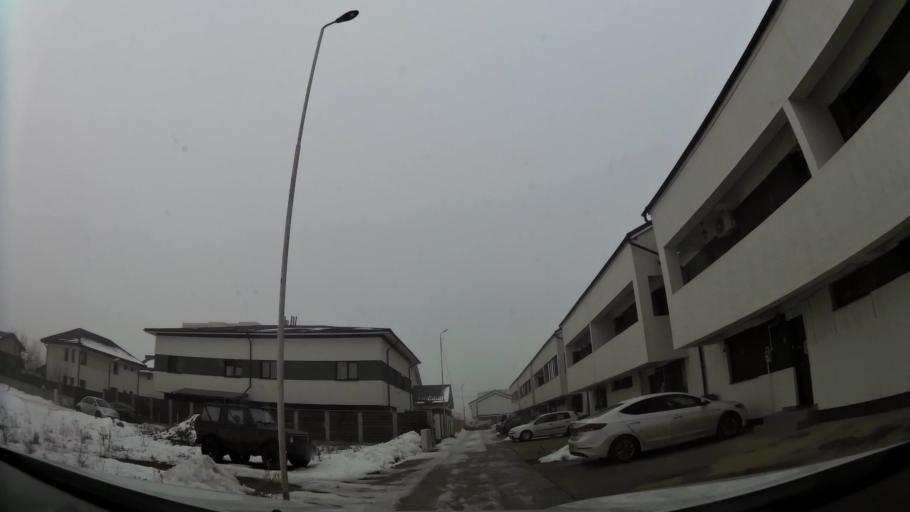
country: RO
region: Ilfov
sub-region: Comuna Chiajna
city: Rosu
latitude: 44.4431
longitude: 25.9975
